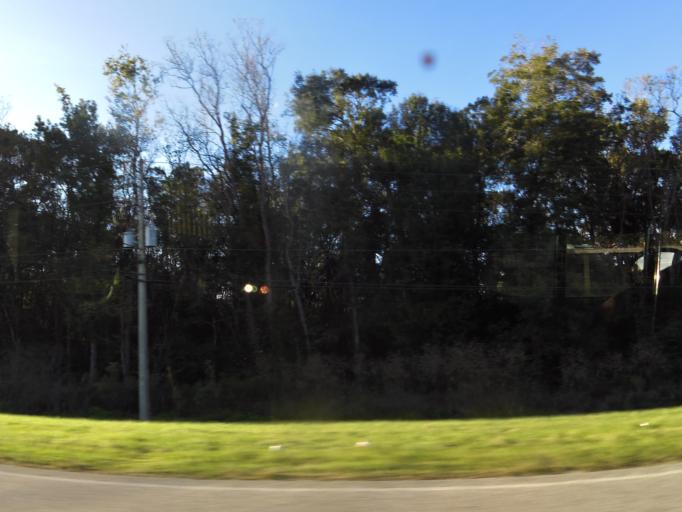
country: US
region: Florida
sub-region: Duval County
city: Jacksonville
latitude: 30.3290
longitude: -81.7673
